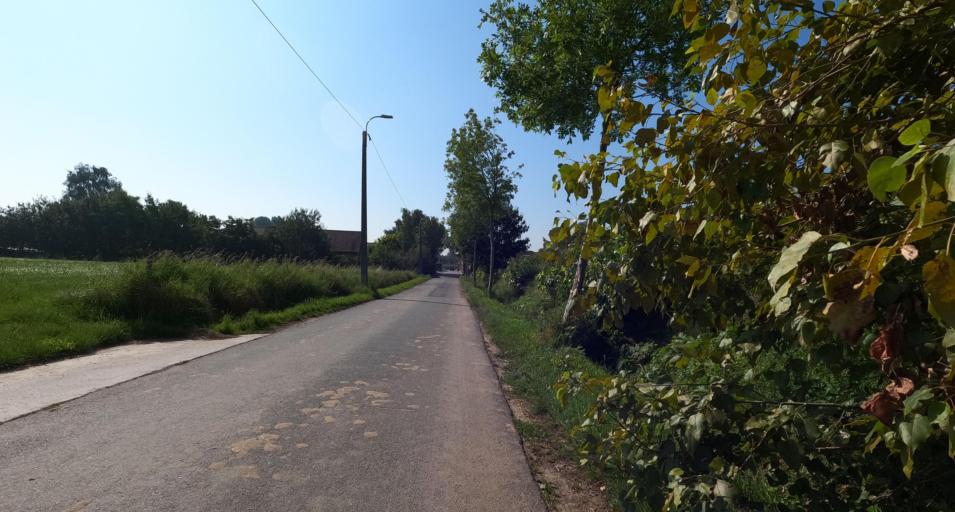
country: BE
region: Flanders
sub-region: Provincie Oost-Vlaanderen
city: Temse
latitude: 51.1486
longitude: 4.2247
